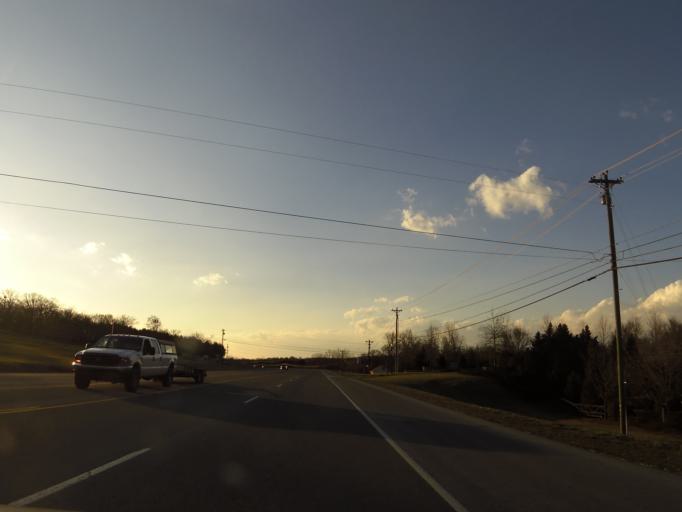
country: US
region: Tennessee
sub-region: Wilson County
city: Lebanon
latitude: 36.2362
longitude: -86.3913
